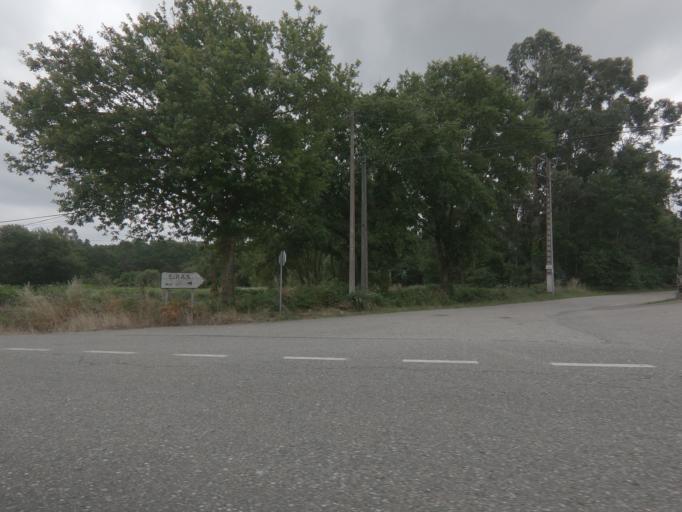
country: PT
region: Viana do Castelo
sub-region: Vila Nova de Cerveira
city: Vila Nova de Cerveira
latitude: 41.9394
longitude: -8.7854
